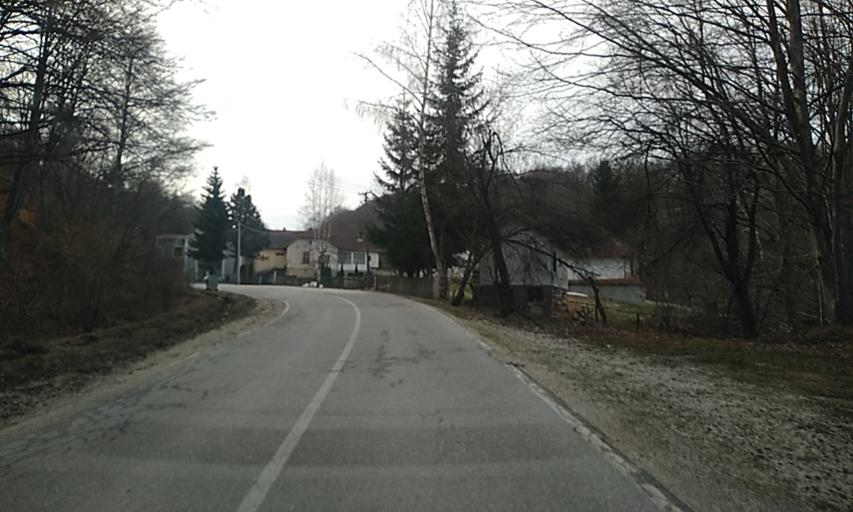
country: RS
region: Central Serbia
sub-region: Jablanicki Okrug
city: Crna Trava
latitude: 42.6808
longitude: 22.3657
